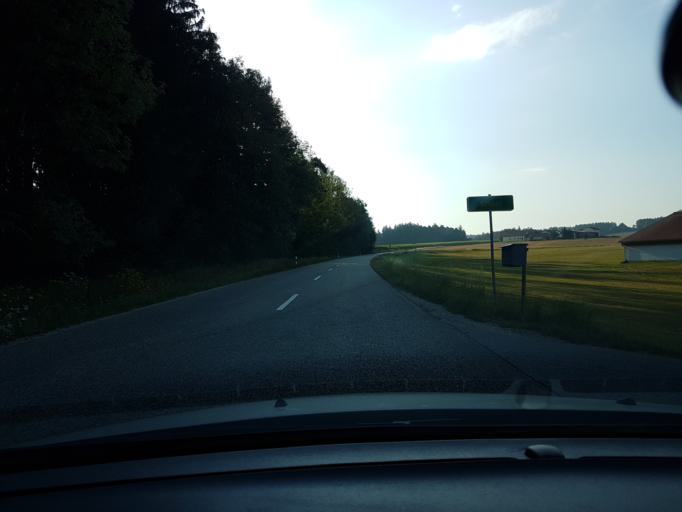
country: DE
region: Bavaria
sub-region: Lower Bavaria
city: Aham
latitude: 48.4958
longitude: 12.4583
